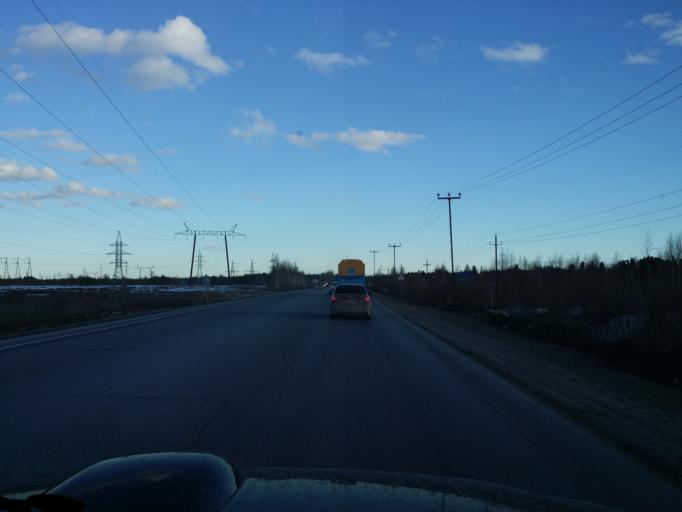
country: RU
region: Khanty-Mansiyskiy Avtonomnyy Okrug
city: Nizhnevartovsk
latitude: 61.0319
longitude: 76.3609
